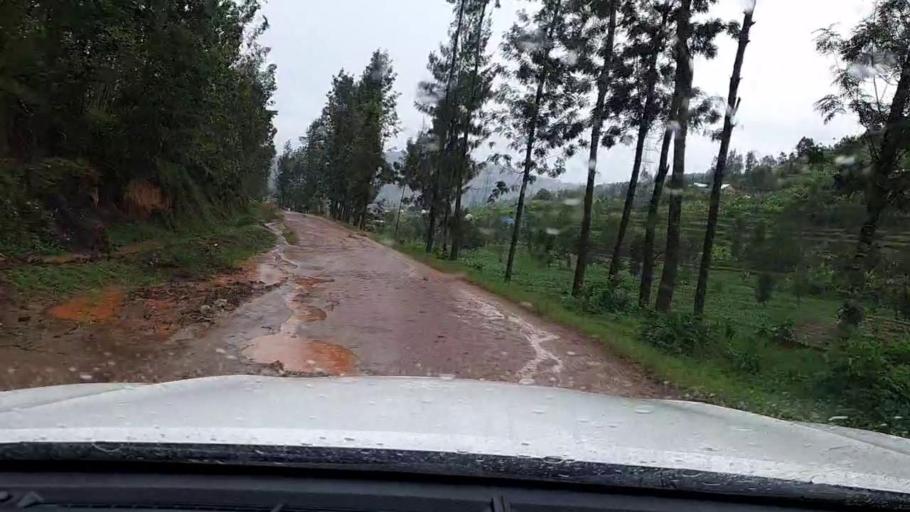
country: RW
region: Northern Province
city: Byumba
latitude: -1.7282
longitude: 29.9354
